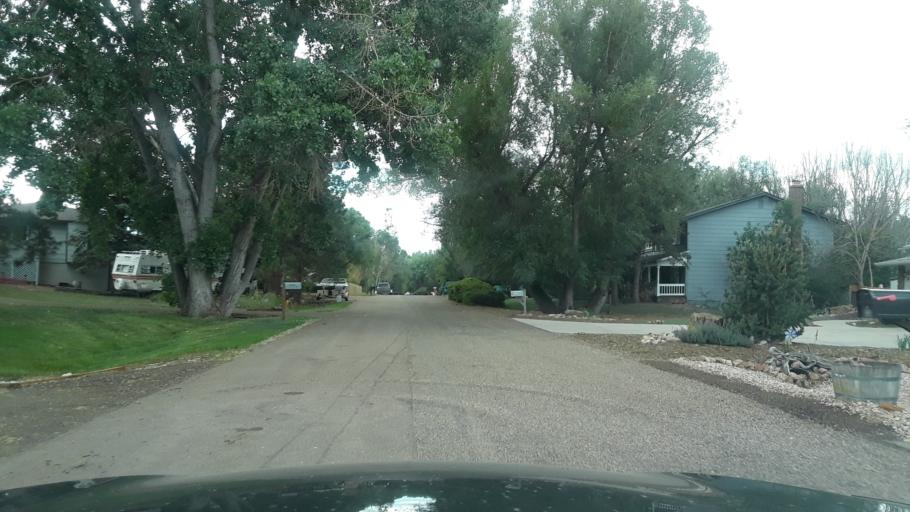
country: US
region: Colorado
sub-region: El Paso County
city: Air Force Academy
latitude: 38.9482
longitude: -104.8267
